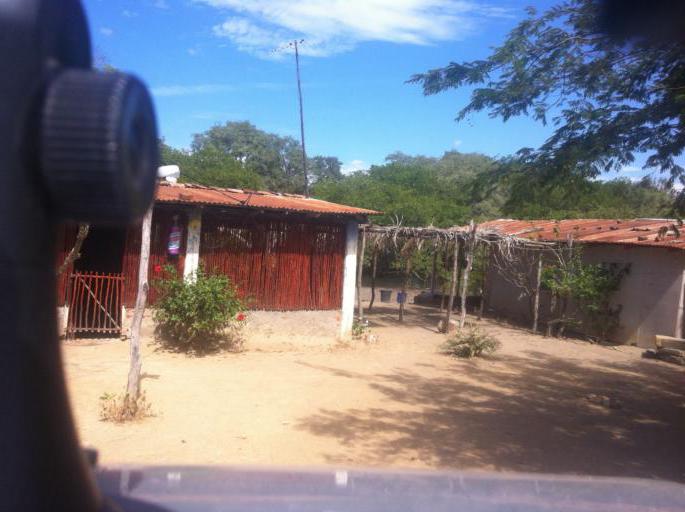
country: NI
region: Rivas
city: Tola
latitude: 11.4771
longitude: -86.1165
